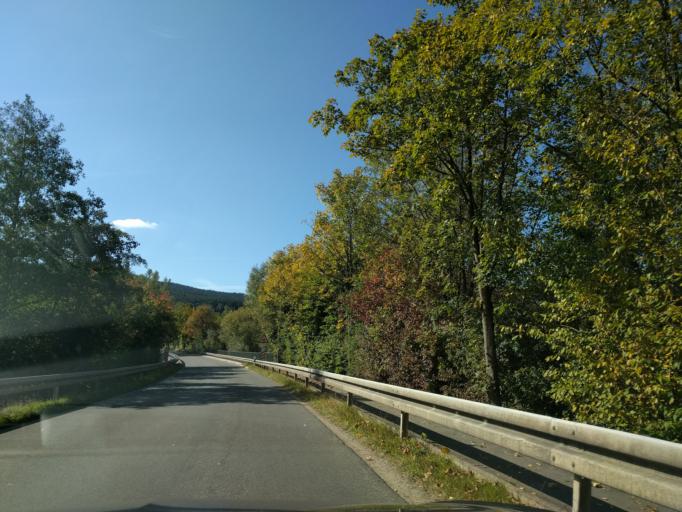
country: DE
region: Bavaria
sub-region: Upper Palatinate
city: Hohenwarth
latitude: 49.2070
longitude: 12.9269
